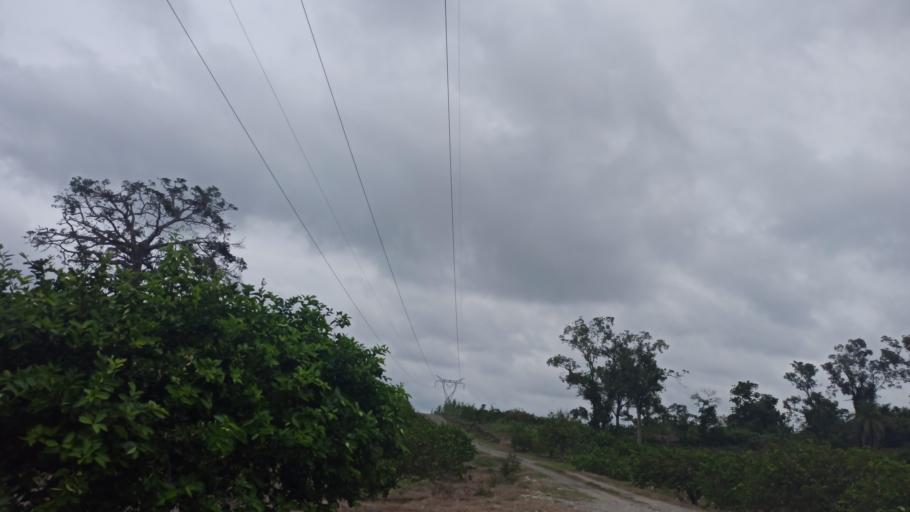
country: MX
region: Puebla
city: Espinal
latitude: 20.2949
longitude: -97.3996
